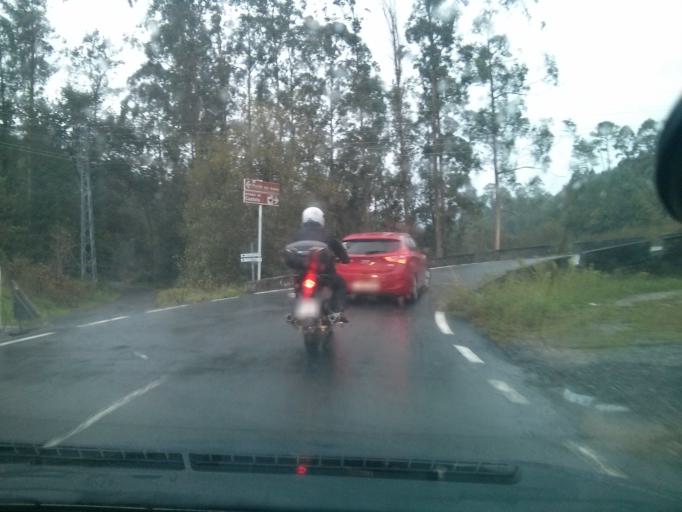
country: ES
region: Galicia
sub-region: Provincia da Coruna
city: Outes
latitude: 42.8342
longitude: -8.8743
